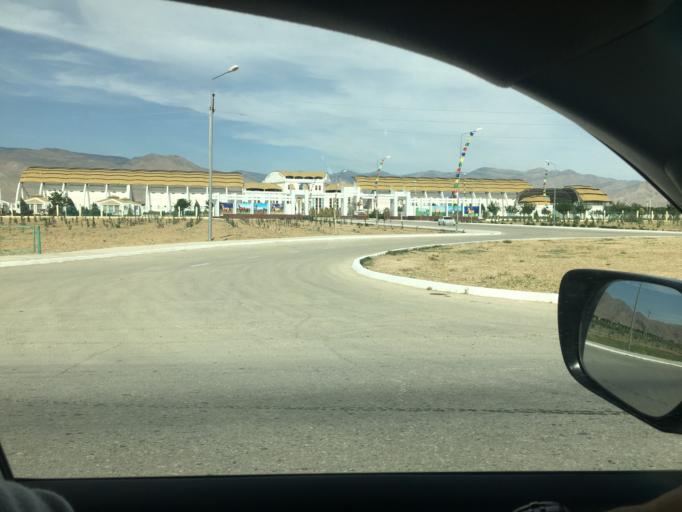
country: TM
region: Balkan
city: Balkanabat
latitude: 39.5733
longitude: 54.2701
